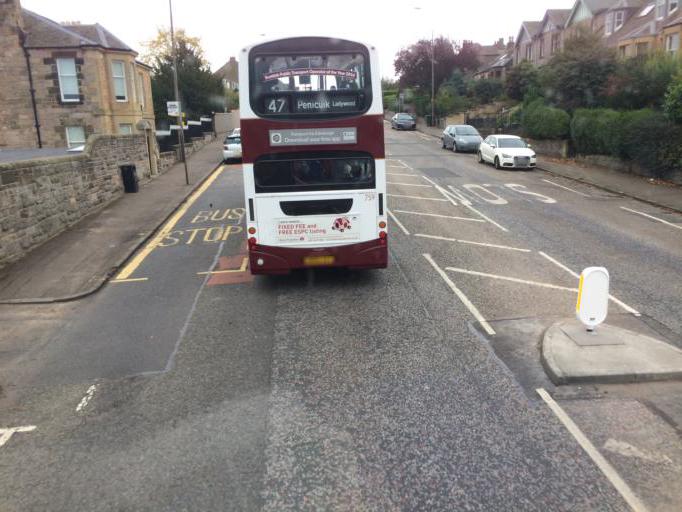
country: GB
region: Scotland
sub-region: Midlothian
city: Loanhead
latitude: 55.9159
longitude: -3.1669
